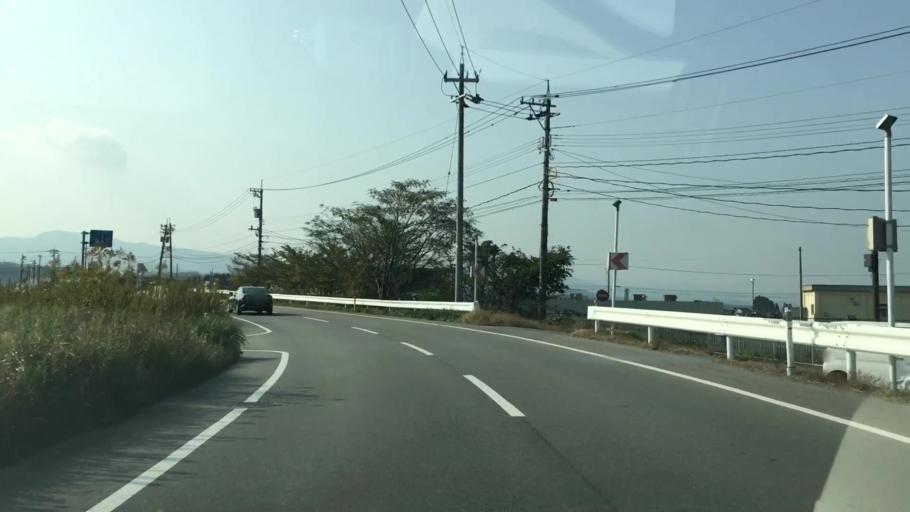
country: JP
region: Toyama
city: Toyama-shi
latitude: 36.6196
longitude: 137.2881
